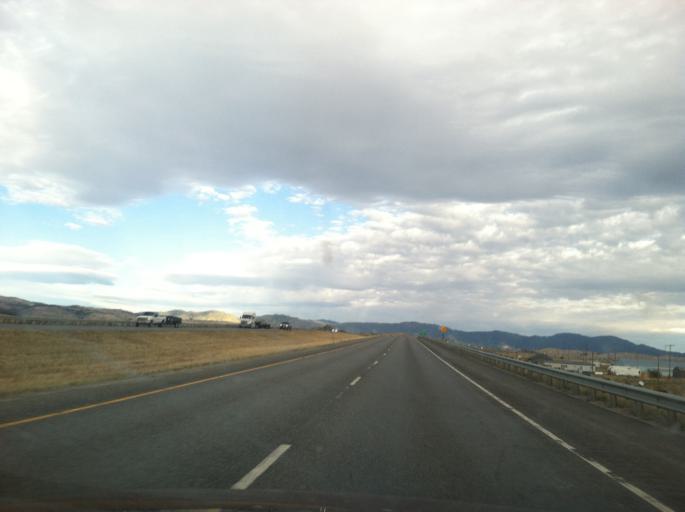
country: US
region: Montana
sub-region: Silver Bow County
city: Butte-Silver Bow (Balance)
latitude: 46.0099
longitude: -112.6943
